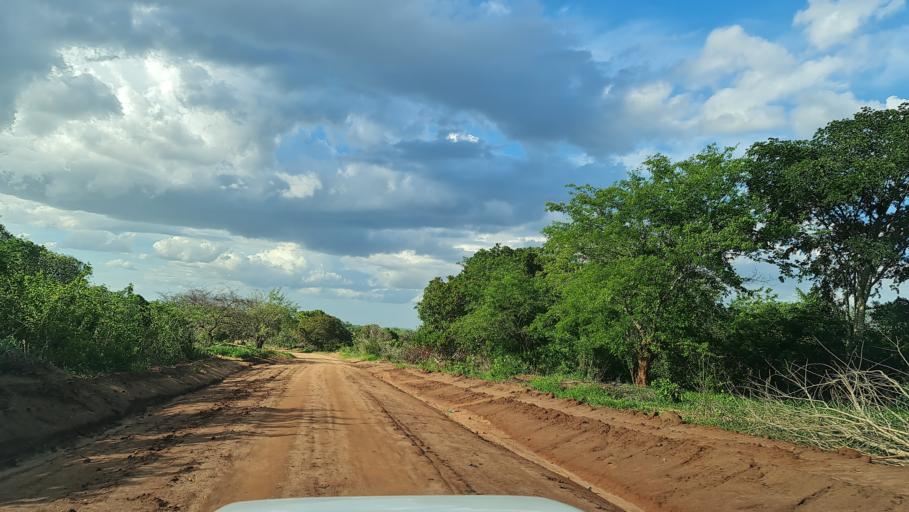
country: MZ
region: Cabo Delgado
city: Pemba
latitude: -13.5521
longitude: 40.1032
